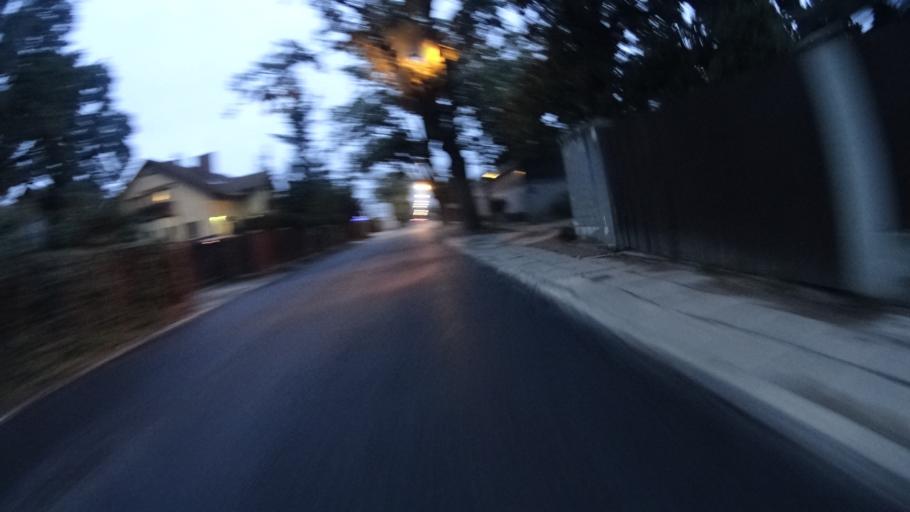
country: PL
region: Masovian Voivodeship
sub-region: Warszawa
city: Ursus
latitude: 52.2214
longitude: 20.8959
